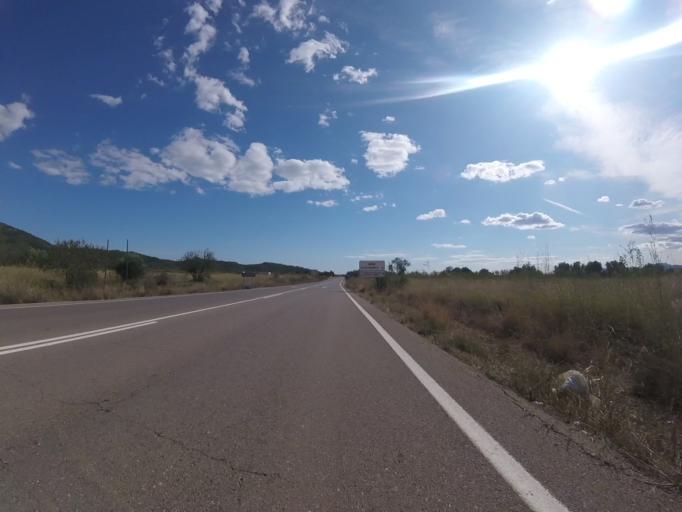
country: ES
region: Valencia
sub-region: Provincia de Castello
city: Alcala de Xivert
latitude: 40.2651
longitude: 0.2421
